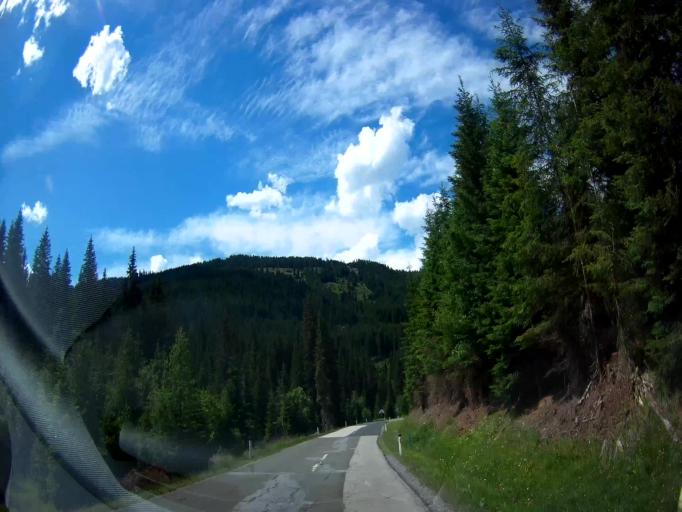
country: AT
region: Styria
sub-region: Politischer Bezirk Murau
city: Stadl an der Mur
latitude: 46.9767
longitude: 14.0073
